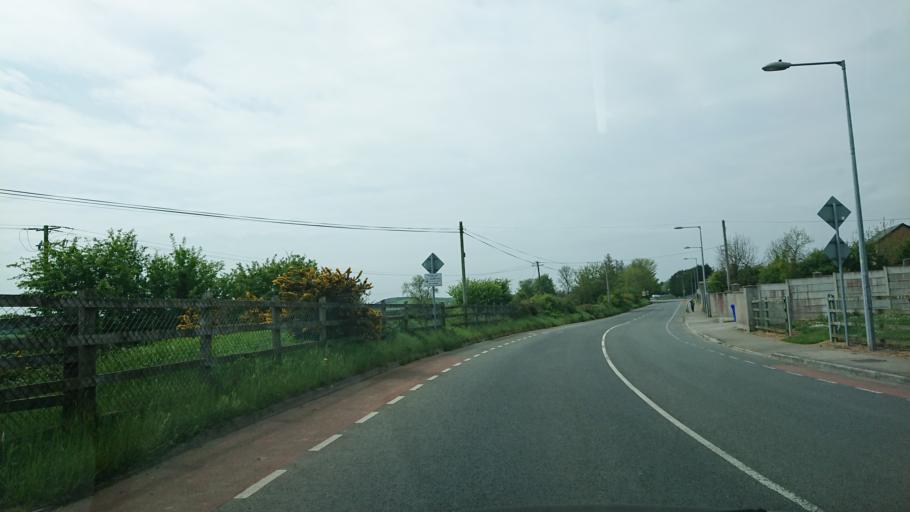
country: IE
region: Munster
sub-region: Waterford
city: Waterford
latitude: 52.2285
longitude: -7.0619
